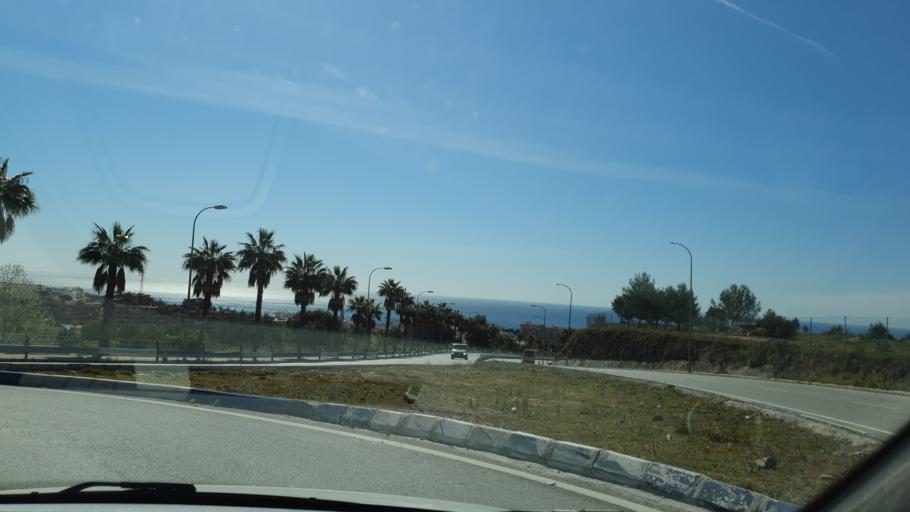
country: ES
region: Andalusia
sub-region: Provincia de Malaga
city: Marbella
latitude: 36.5278
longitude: -4.8820
